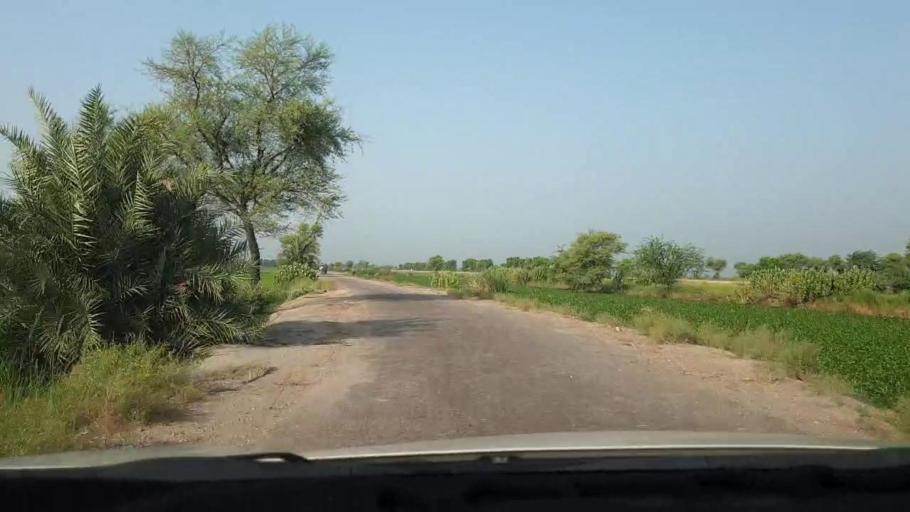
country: PK
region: Sindh
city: Larkana
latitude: 27.5112
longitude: 68.1844
